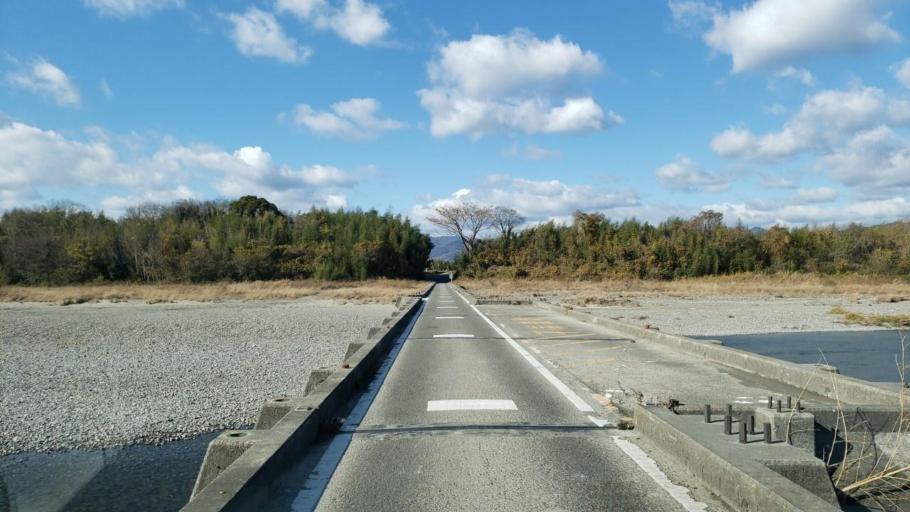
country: JP
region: Tokushima
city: Kamojimacho-jogejima
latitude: 34.0688
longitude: 134.3178
